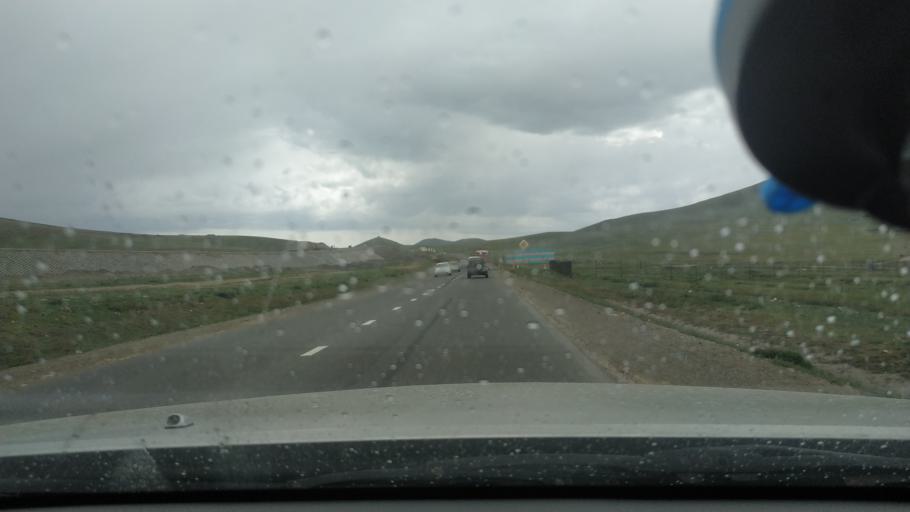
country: MN
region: Ulaanbaatar
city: Ulaanbaatar
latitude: 47.7989
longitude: 106.7461
